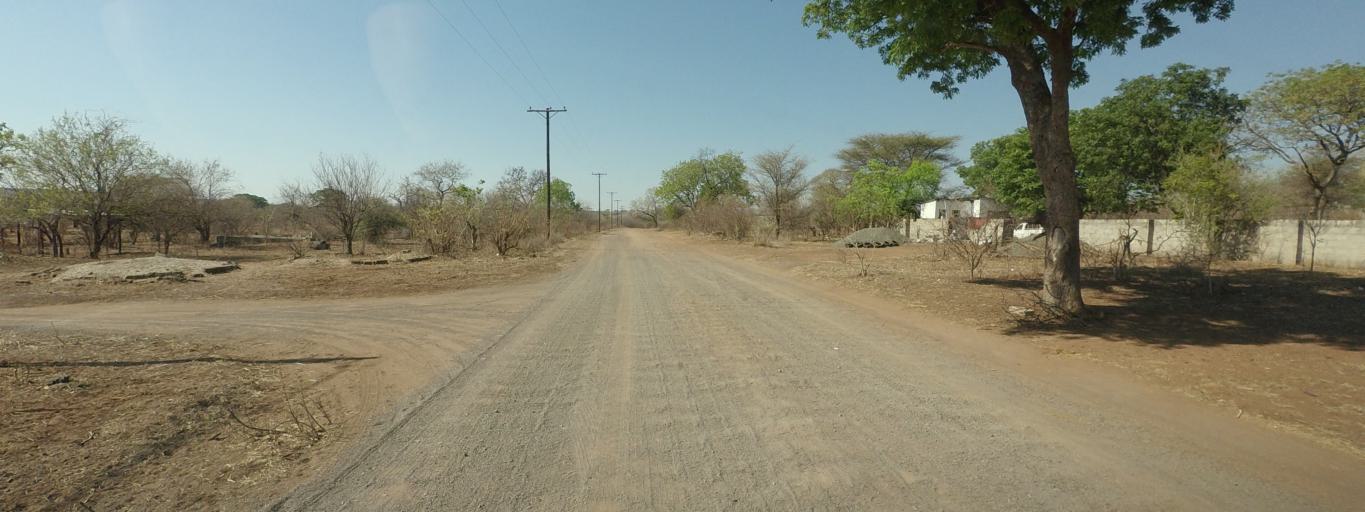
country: BW
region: North West
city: Kasane
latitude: -17.8955
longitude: 25.2290
